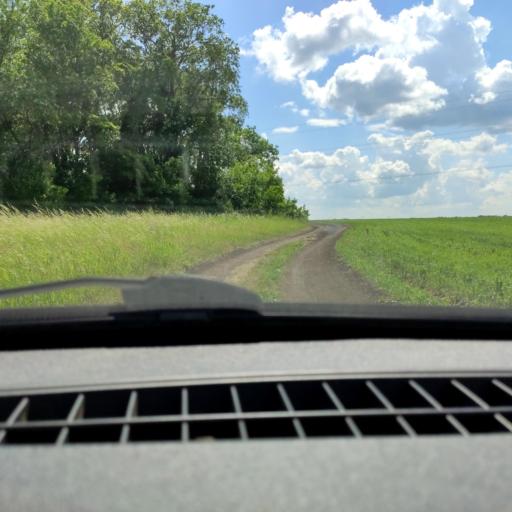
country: RU
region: Bashkortostan
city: Kabakovo
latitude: 54.5166
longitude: 56.0919
